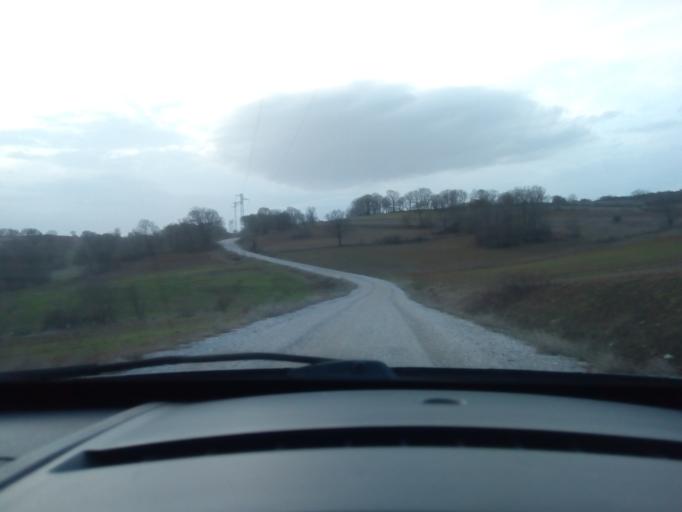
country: TR
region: Balikesir
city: Omerkoy
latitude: 39.8893
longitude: 28.0401
